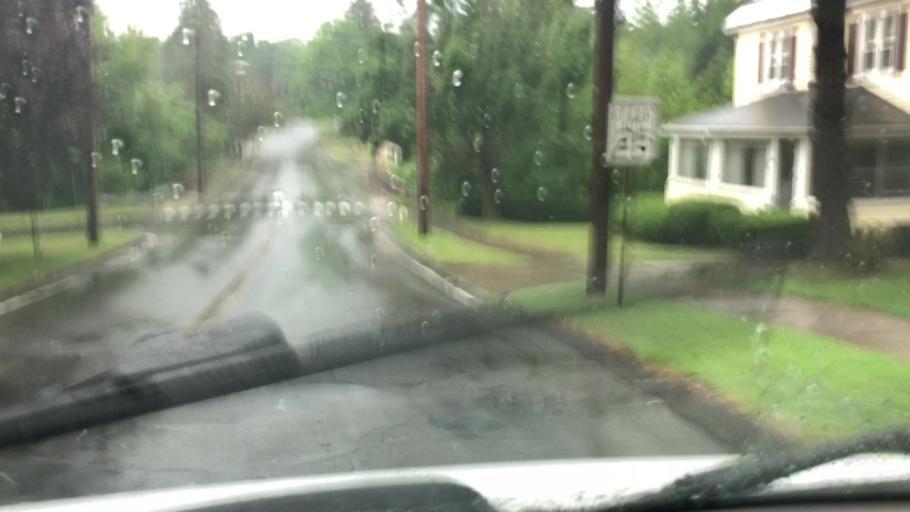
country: US
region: Massachusetts
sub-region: Berkshire County
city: Pittsfield
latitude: 42.4404
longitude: -73.2475
